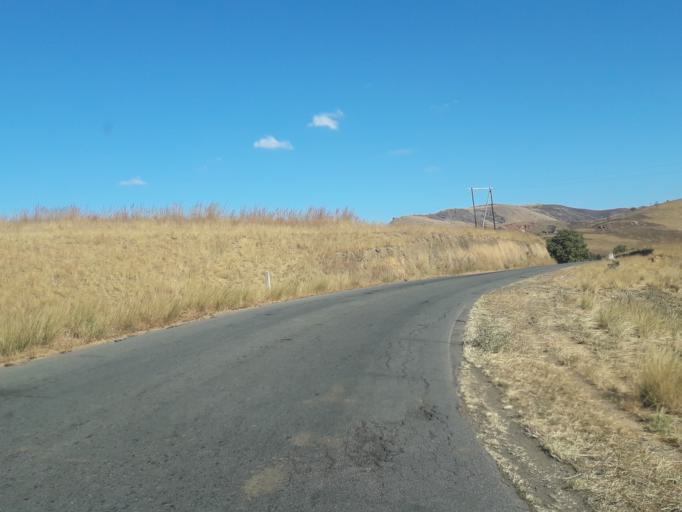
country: MG
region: Betsiboka
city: Maevatanana
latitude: -17.6221
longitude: 46.9449
